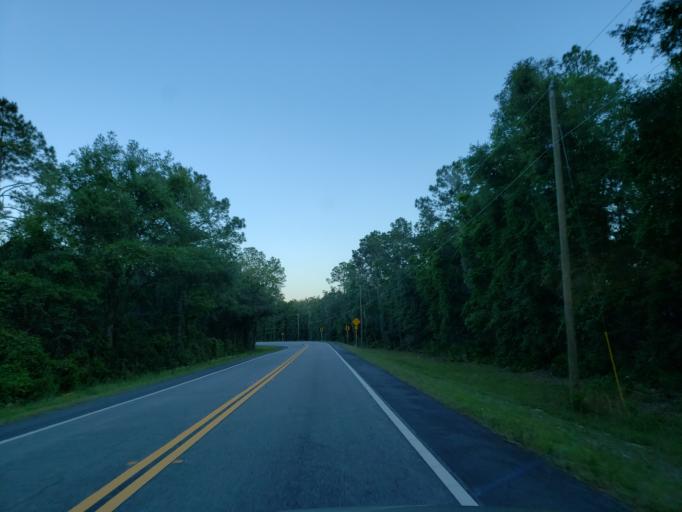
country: US
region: Georgia
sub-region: Echols County
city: Statenville
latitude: 30.5601
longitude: -83.1360
